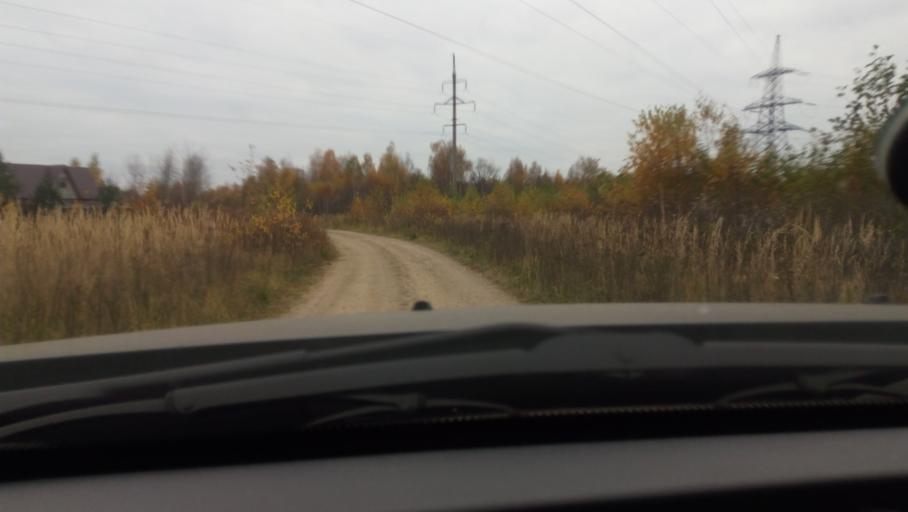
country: RU
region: Moskovskaya
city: Avsyunino
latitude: 55.5816
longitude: 39.2497
